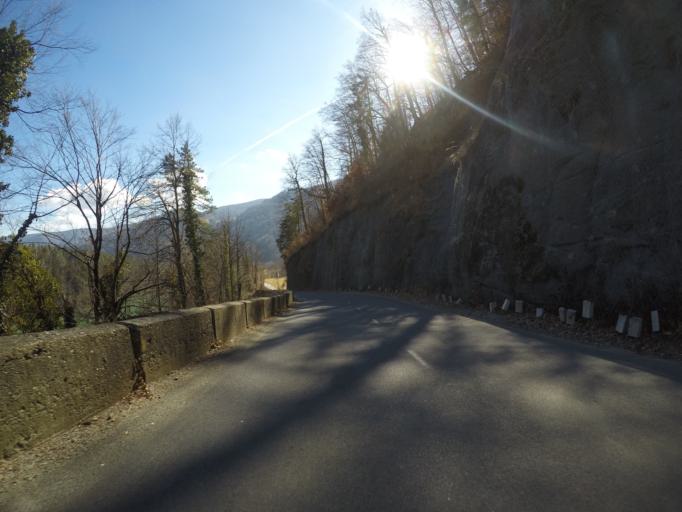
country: SI
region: Selnica ob Dravi
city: Selnica ob Dravi
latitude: 46.5408
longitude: 15.4514
